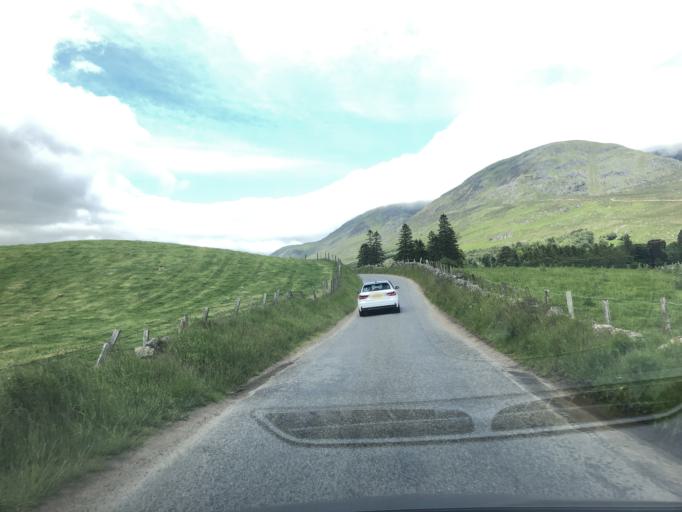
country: GB
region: Scotland
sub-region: Angus
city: Kirriemuir
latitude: 56.8397
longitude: -3.1042
